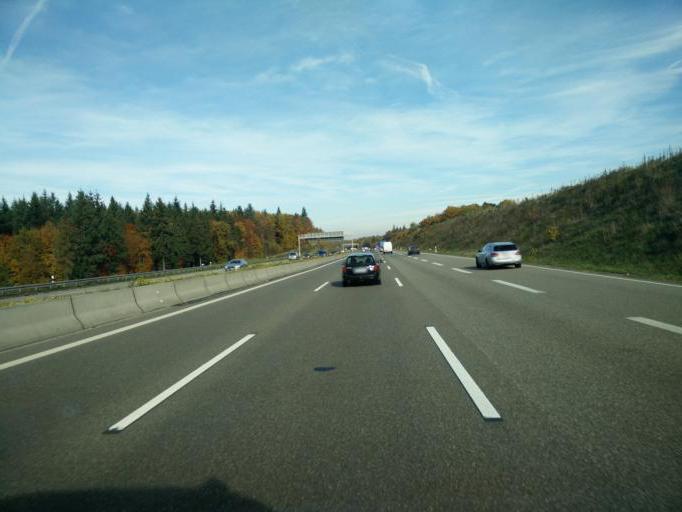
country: DE
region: Baden-Wuerttemberg
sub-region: Karlsruhe Region
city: Wurmberg
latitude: 48.8810
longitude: 8.7883
